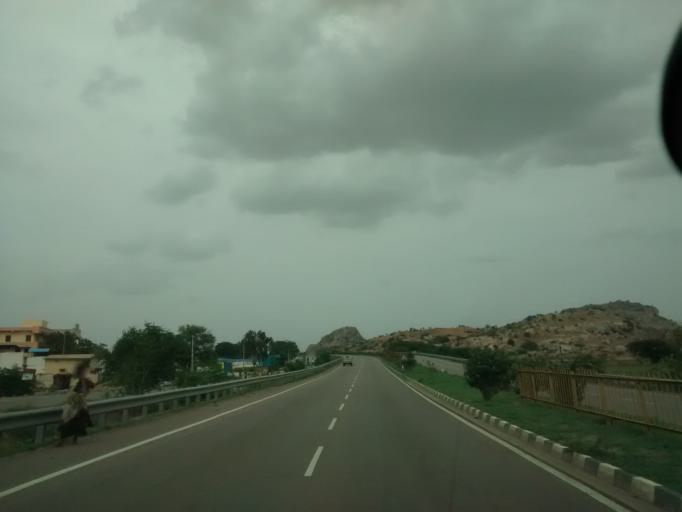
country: IN
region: Andhra Pradesh
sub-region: Kurnool
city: Ramapuram
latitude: 15.1588
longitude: 77.6709
